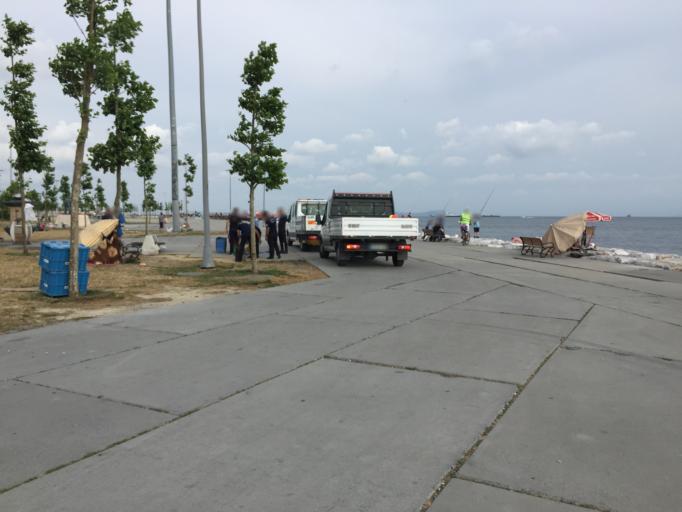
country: TR
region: Istanbul
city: Istanbul
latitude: 40.9978
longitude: 28.9408
